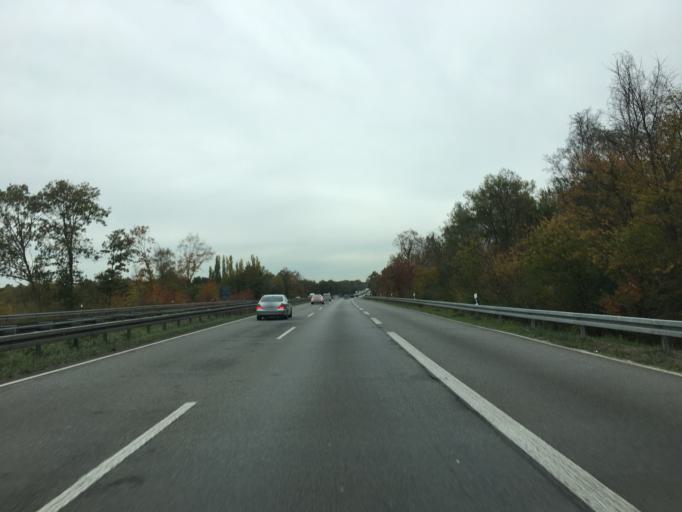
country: NL
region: Gelderland
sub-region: Gemeente Montferland
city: s-Heerenberg
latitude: 51.8832
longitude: 6.1819
